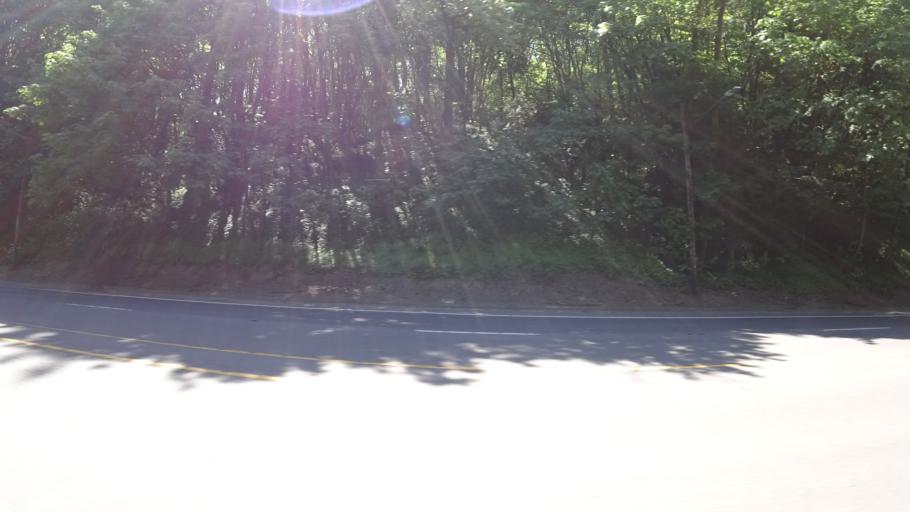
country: US
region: Oregon
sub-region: Multnomah County
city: Portland
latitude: 45.4855
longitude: -122.6819
